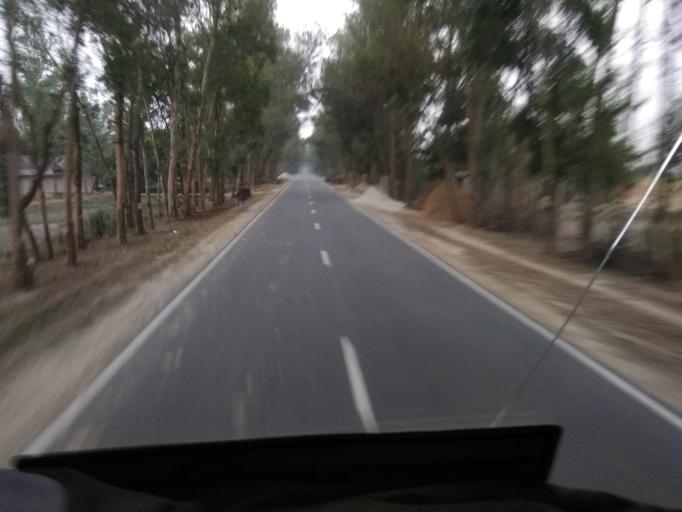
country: BD
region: Rajshahi
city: Bogra
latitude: 24.6620
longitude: 89.2690
